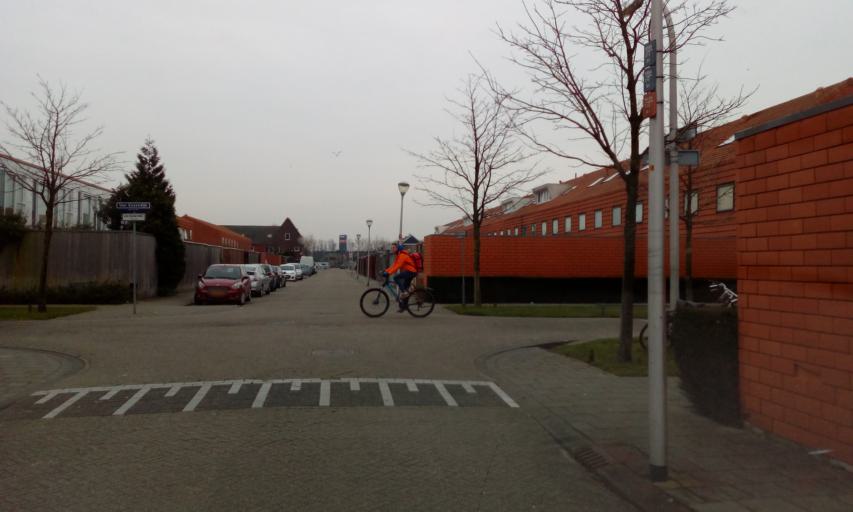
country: NL
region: South Holland
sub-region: Gemeente Den Haag
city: Ypenburg
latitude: 52.0340
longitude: 4.3632
